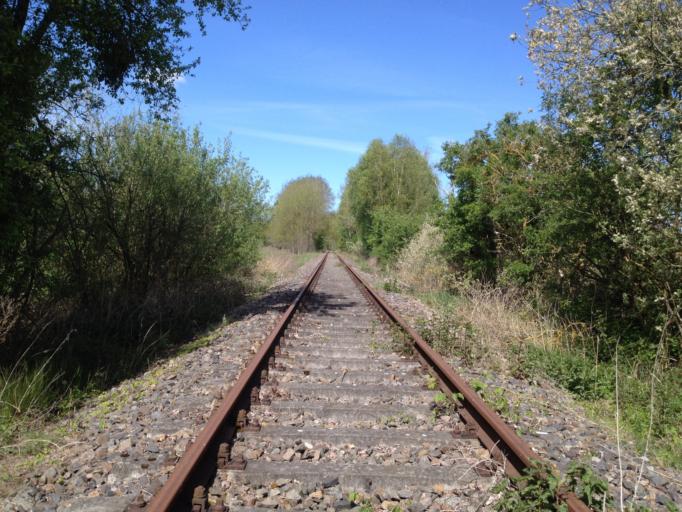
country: DE
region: Brandenburg
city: Templin
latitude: 53.1322
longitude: 13.4361
